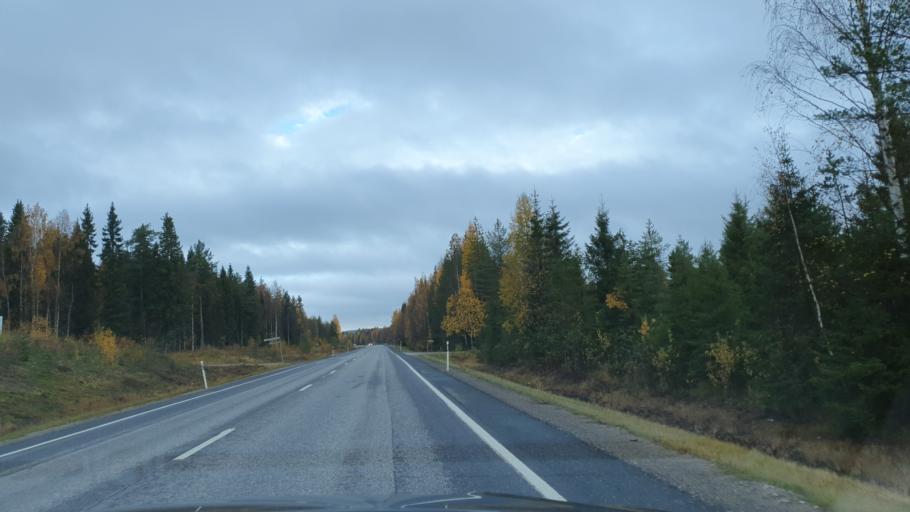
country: FI
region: Lapland
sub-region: Rovaniemi
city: Rovaniemi
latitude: 66.5686
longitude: 25.6372
